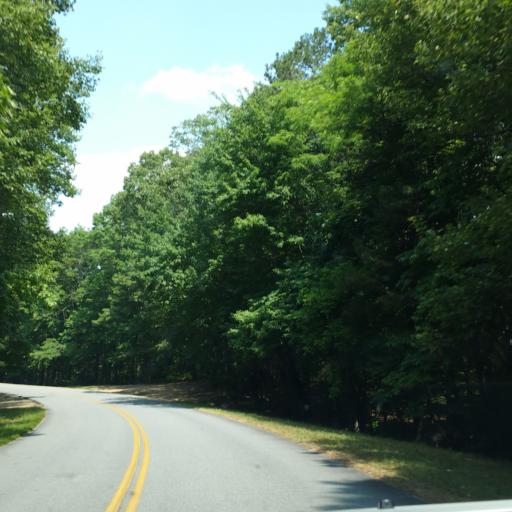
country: US
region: North Carolina
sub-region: Buncombe County
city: Avery Creek
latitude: 35.4975
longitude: -82.5685
